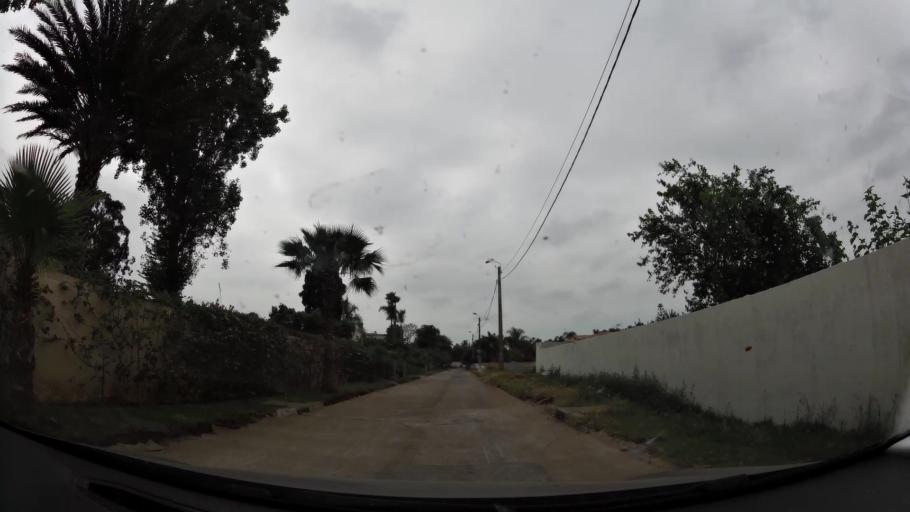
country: MA
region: Rabat-Sale-Zemmour-Zaer
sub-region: Rabat
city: Rabat
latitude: 33.9633
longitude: -6.8169
